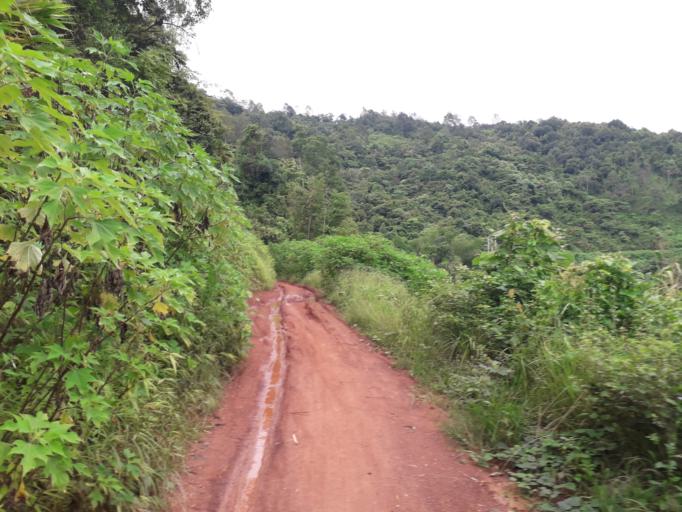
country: CN
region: Yunnan
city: Menglie
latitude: 22.2407
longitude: 101.6132
